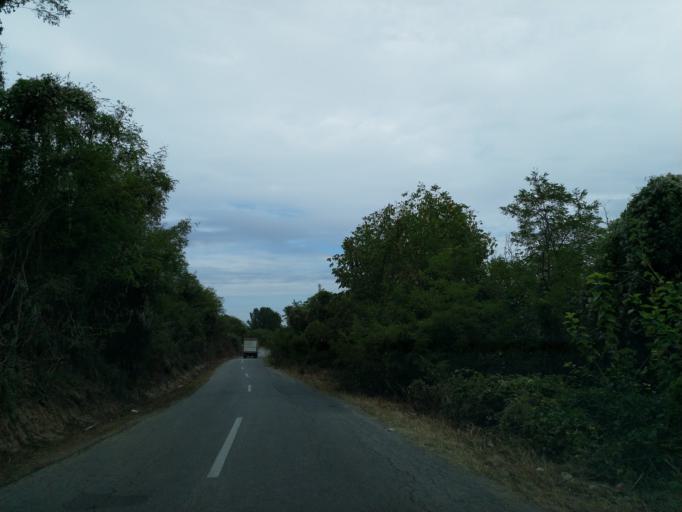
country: RS
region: Central Serbia
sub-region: Pomoravski Okrug
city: Paracin
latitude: 43.8555
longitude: 21.3244
